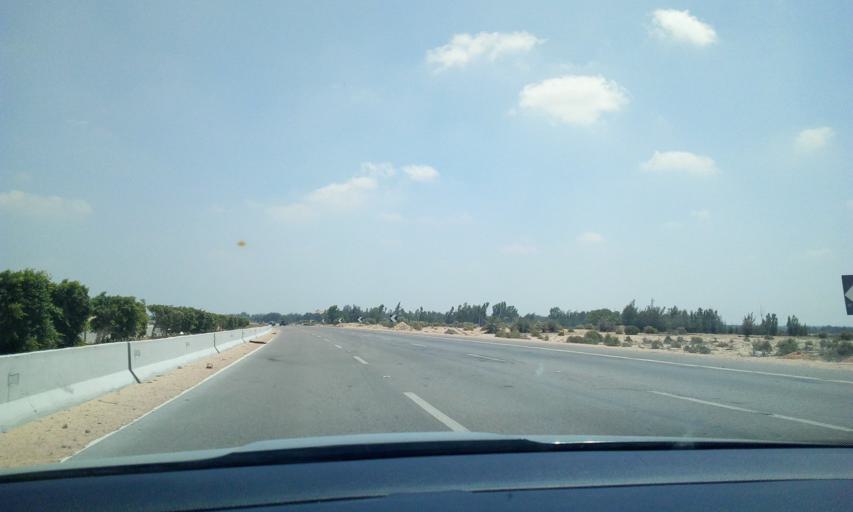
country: EG
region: Al Buhayrah
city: Beheira
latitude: 30.4830
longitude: 30.1880
